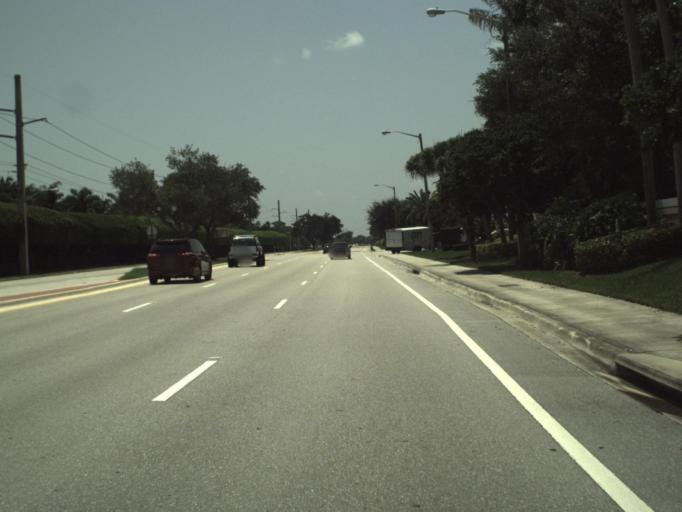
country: US
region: Florida
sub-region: Palm Beach County
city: Kings Point
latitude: 26.4068
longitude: -80.1464
